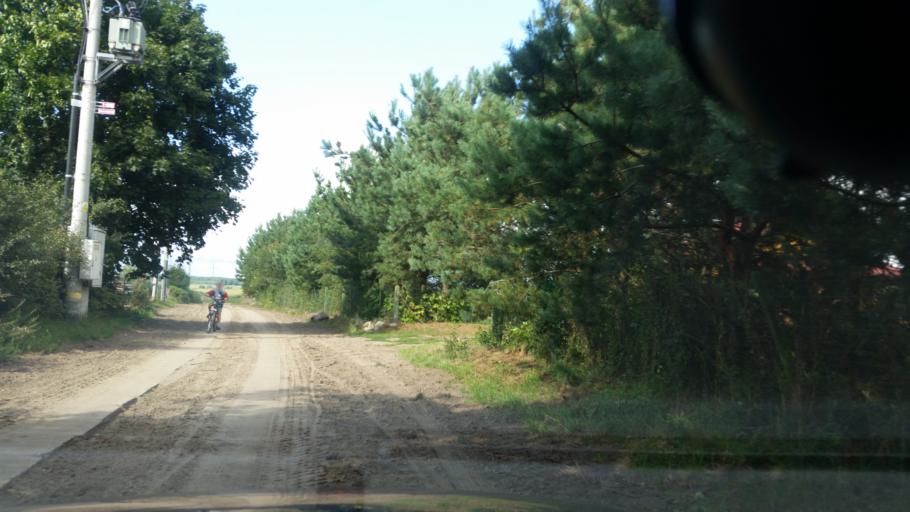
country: PL
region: Pomeranian Voivodeship
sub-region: Powiat wejherowski
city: Choczewo
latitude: 54.7706
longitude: 17.7961
